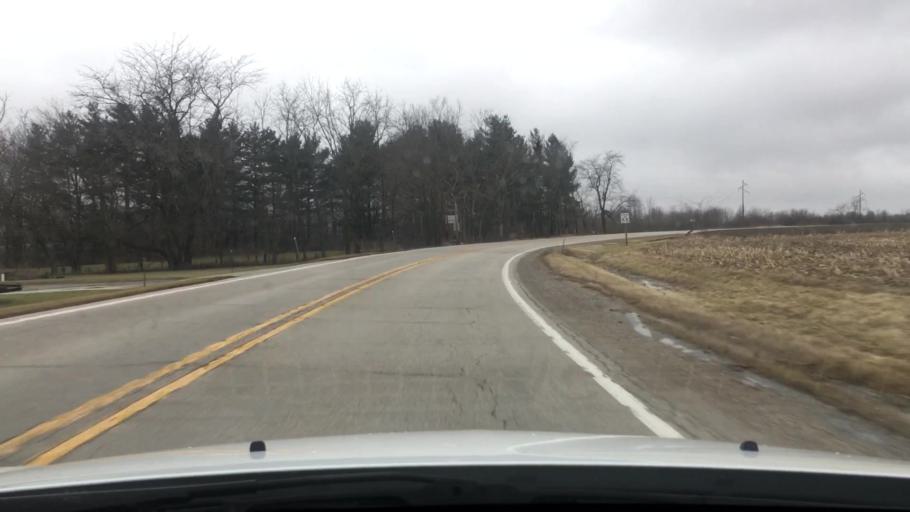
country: US
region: Illinois
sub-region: Iroquois County
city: Sheldon
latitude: 40.8292
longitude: -87.5857
